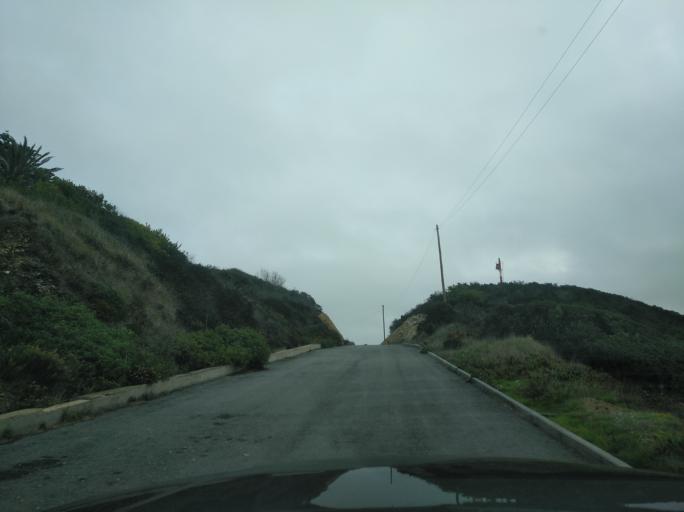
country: PT
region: Beja
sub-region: Odemira
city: Sao Teotonio
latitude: 37.5521
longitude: -8.7916
